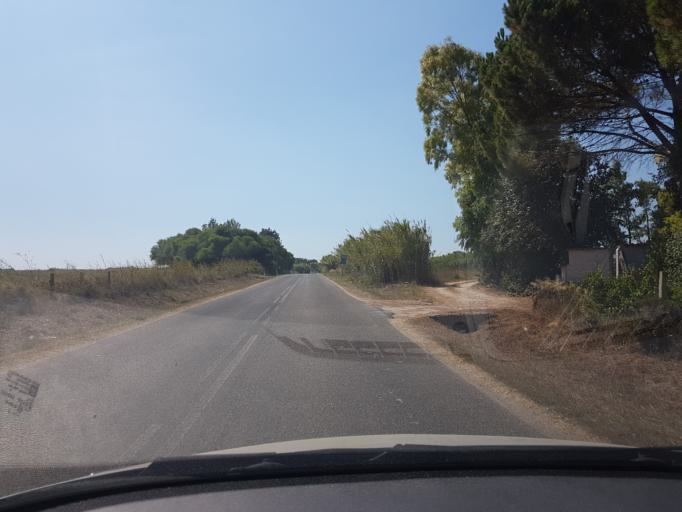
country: IT
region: Sardinia
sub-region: Provincia di Oristano
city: Riola Sardo
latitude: 40.0005
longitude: 8.5101
